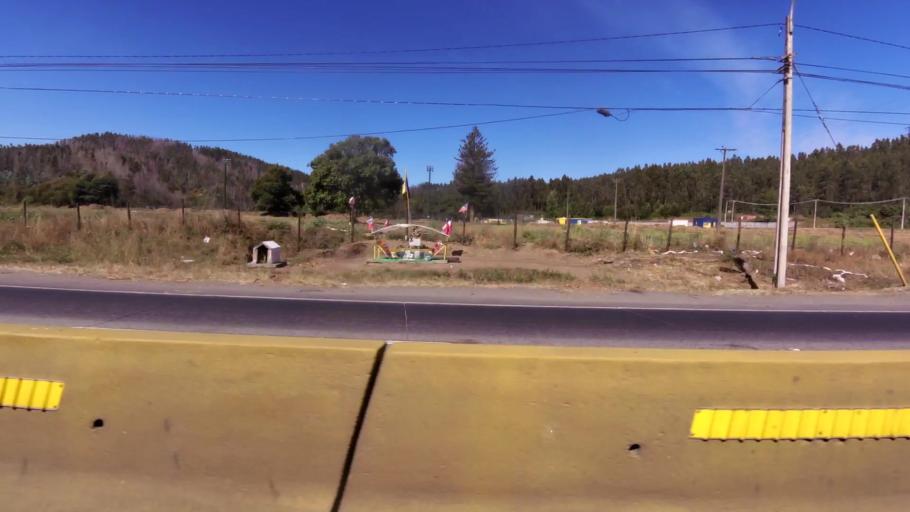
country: CL
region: Biobio
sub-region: Provincia de Concepcion
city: Concepcion
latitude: -36.7976
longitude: -73.0258
